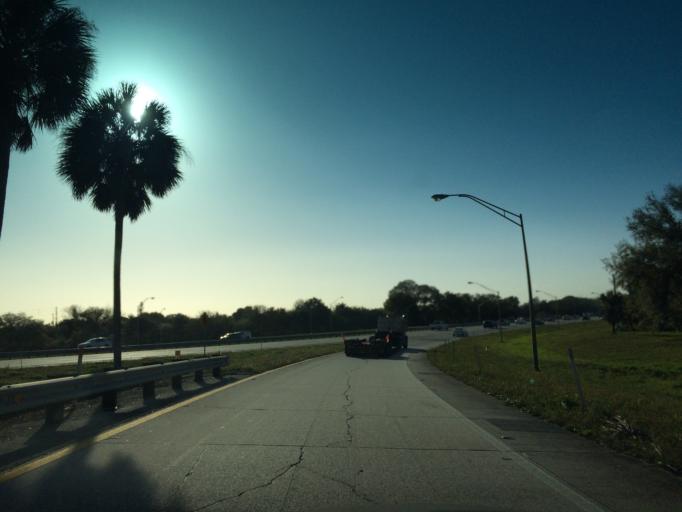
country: US
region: Florida
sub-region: Pinellas County
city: Lealman
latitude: 27.8499
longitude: -82.6647
